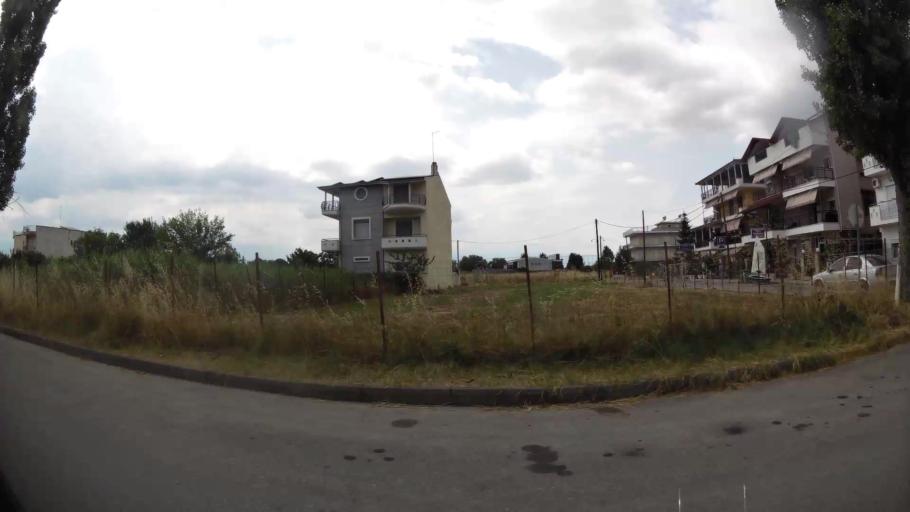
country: GR
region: Central Macedonia
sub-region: Nomos Pierias
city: Paralia
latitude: 40.2667
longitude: 22.5930
